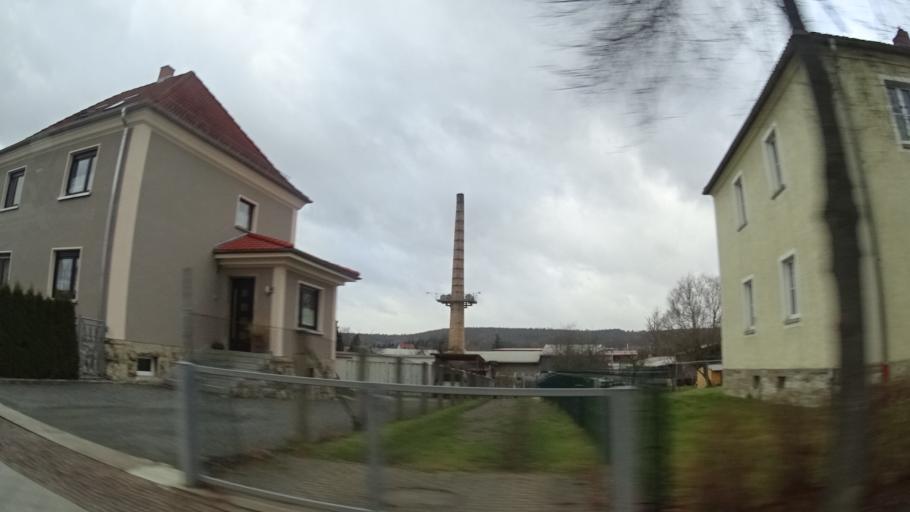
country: DE
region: Thuringia
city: Neustadt (Orla)
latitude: 50.7376
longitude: 11.7385
